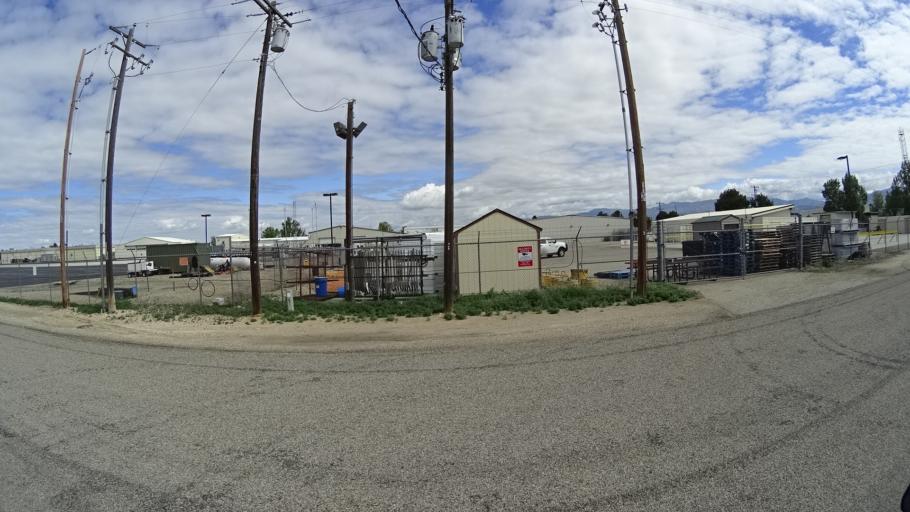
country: US
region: Idaho
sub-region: Ada County
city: Boise
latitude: 43.5641
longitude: -116.2089
